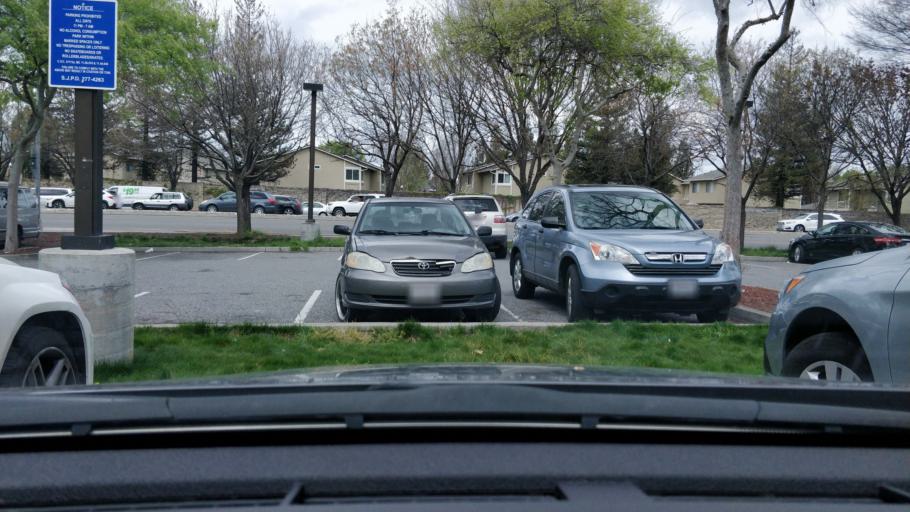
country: US
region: California
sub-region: Santa Clara County
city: Seven Trees
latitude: 37.3114
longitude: -121.8415
